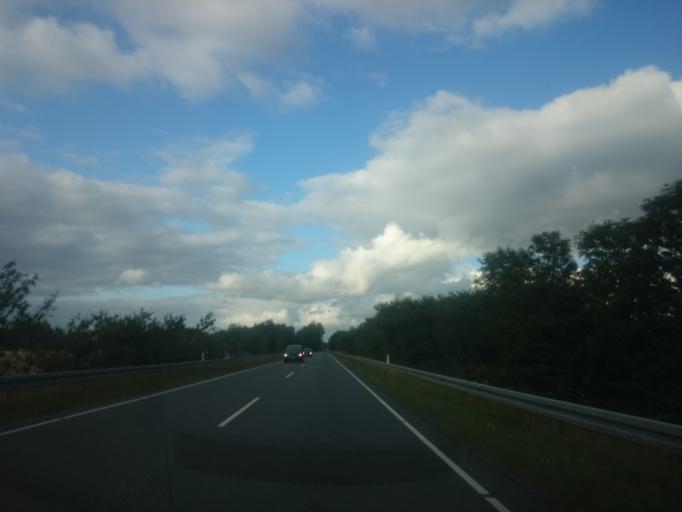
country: DK
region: South Denmark
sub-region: Varde Kommune
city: Olgod
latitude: 55.6618
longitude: 8.7001
